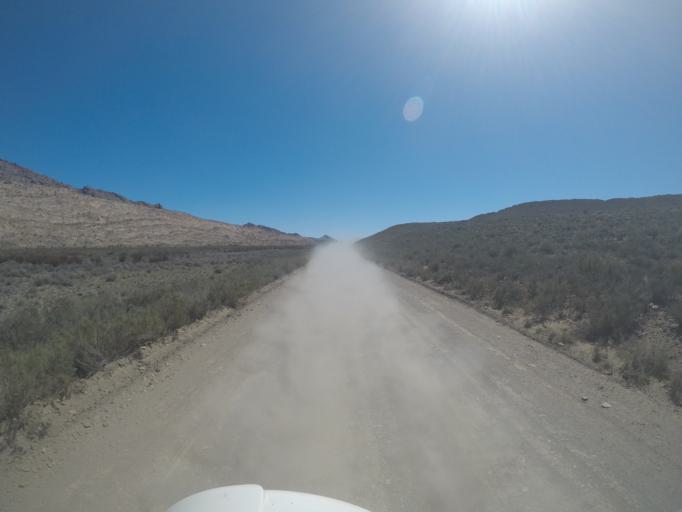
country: ZA
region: Western Cape
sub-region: Cape Winelands District Municipality
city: Ceres
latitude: -32.8255
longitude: 19.4543
